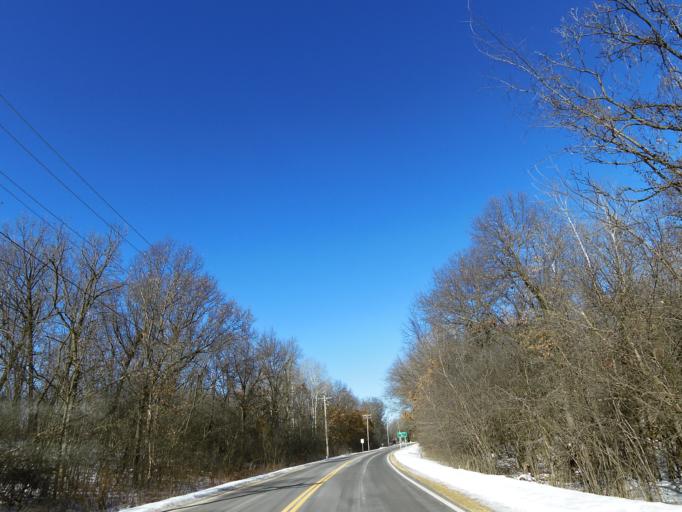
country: US
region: Minnesota
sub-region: Washington County
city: Lake Elmo
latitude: 44.9758
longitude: -92.8632
